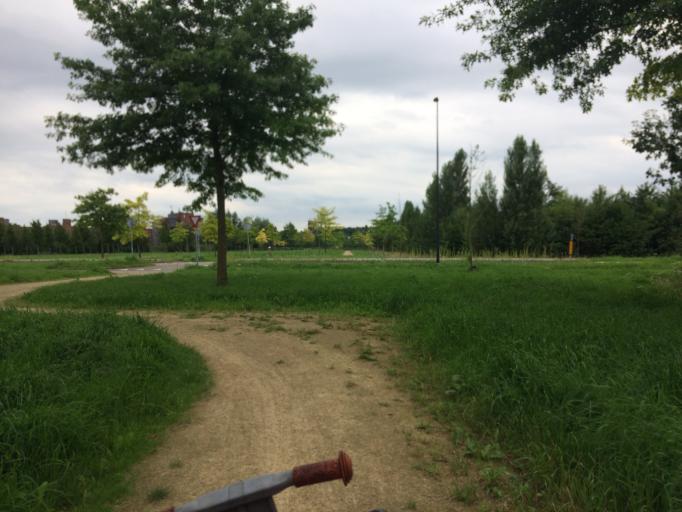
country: NL
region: Gelderland
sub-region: Gemeente Maasdriel
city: Hedel
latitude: 51.7307
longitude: 5.2453
